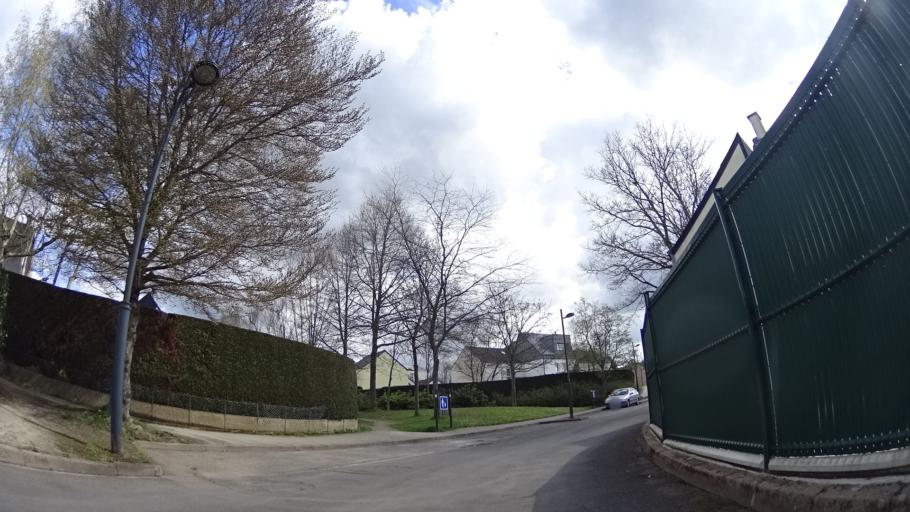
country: FR
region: Brittany
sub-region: Departement d'Ille-et-Vilaine
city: Rennes
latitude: 48.1346
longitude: -1.6688
